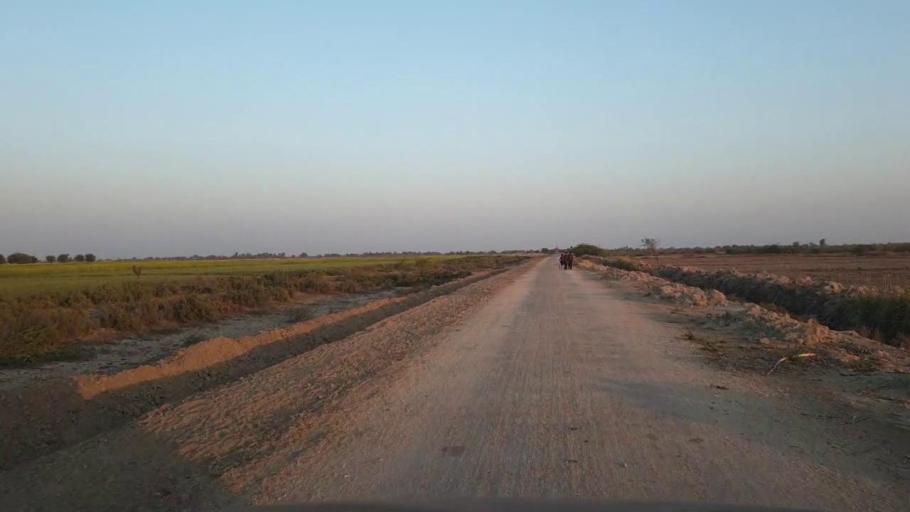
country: PK
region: Sindh
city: Digri
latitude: 25.1393
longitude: 69.2460
